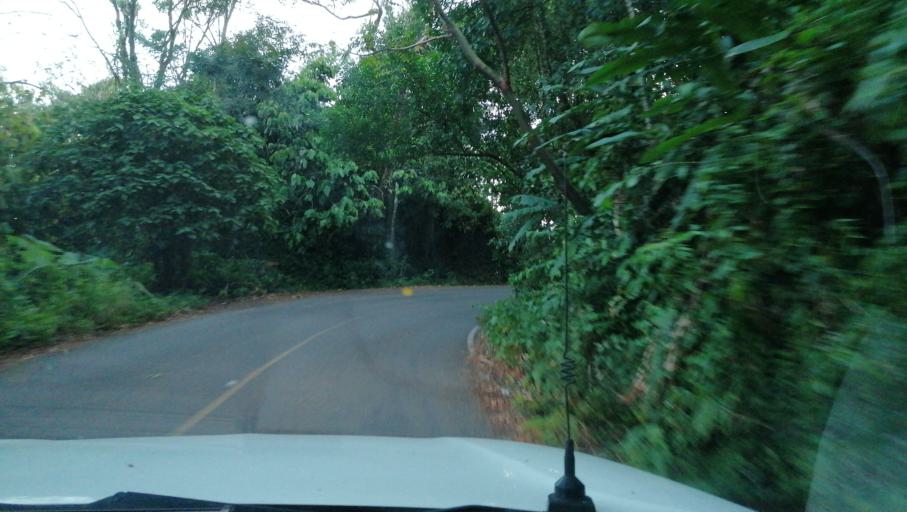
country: MX
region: Chiapas
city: Ostuacan
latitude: 17.4233
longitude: -93.3434
